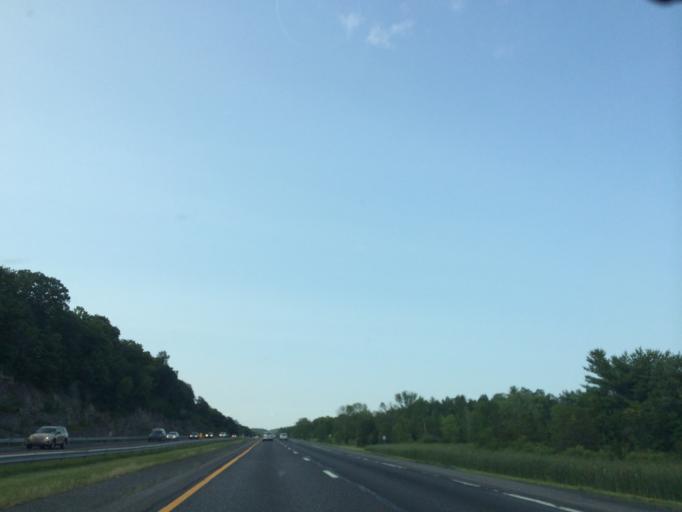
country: US
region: New York
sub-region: Ulster County
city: Saugerties
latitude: 42.1528
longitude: -73.9429
